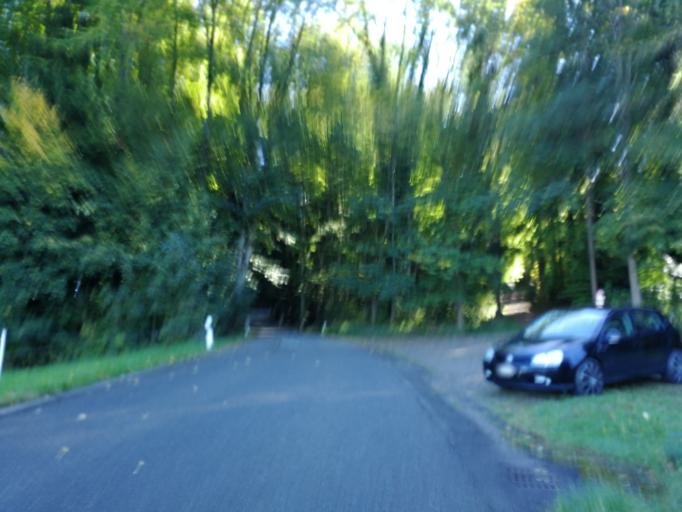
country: CH
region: Zurich
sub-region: Bezirk Uster
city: Aesch
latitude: 47.3203
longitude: 8.6558
